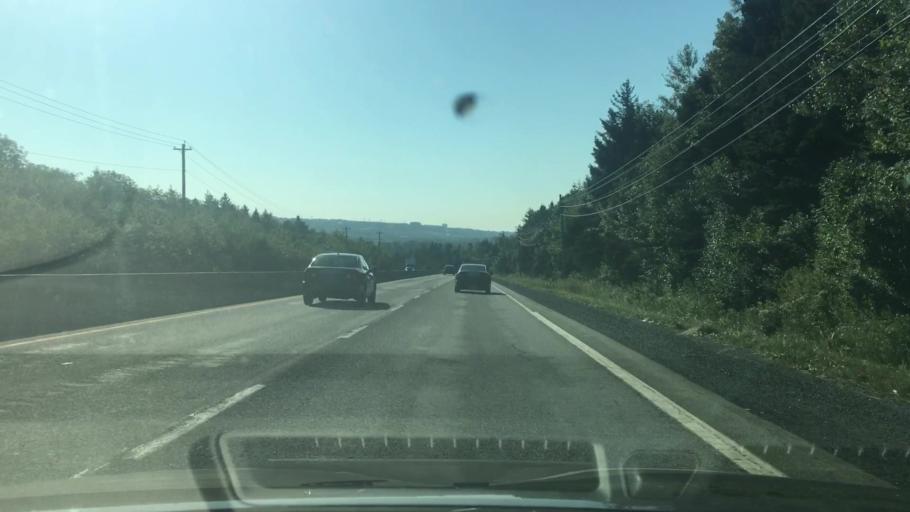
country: CA
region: Nova Scotia
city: Dartmouth
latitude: 44.7112
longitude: -63.6273
